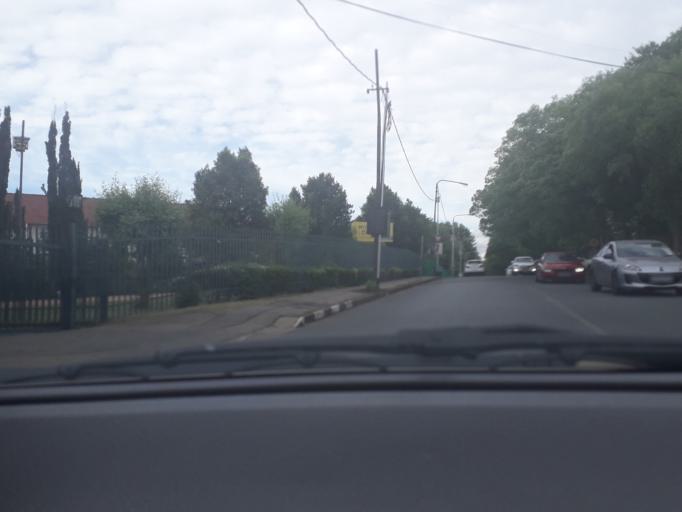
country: ZA
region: Gauteng
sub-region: City of Johannesburg Metropolitan Municipality
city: Johannesburg
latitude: -26.1506
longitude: 28.0233
